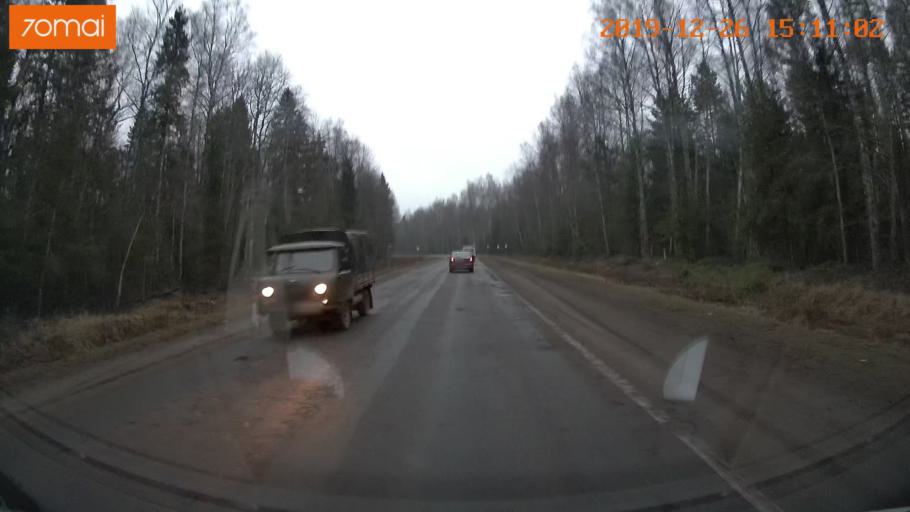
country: RU
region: Jaroslavl
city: Rybinsk
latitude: 58.1365
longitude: 38.8569
